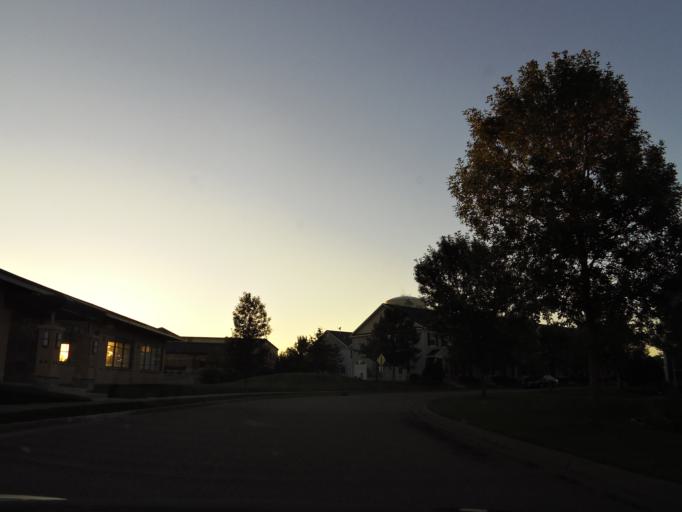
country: US
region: Minnesota
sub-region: Washington County
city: Oakdale
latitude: 44.9653
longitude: -92.9519
